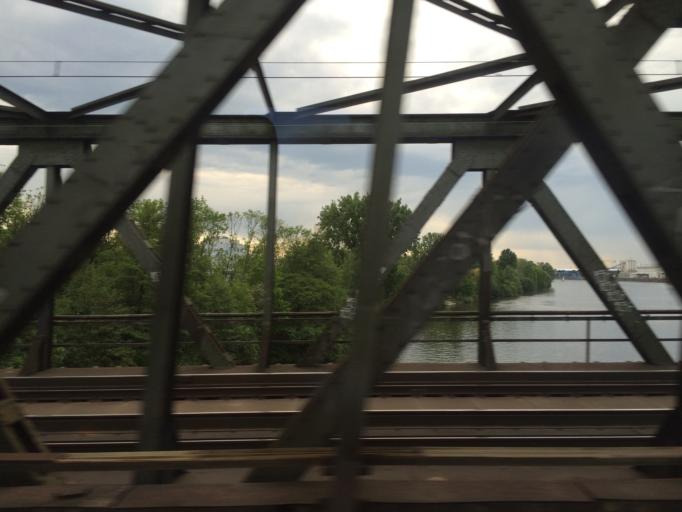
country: DE
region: Hesse
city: Niederrad
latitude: 50.0952
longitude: 8.6544
